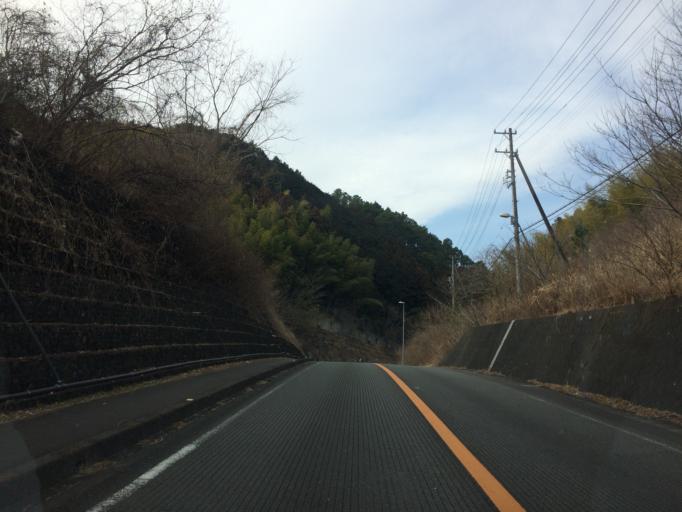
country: JP
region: Shizuoka
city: Fujieda
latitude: 34.9206
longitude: 138.2779
